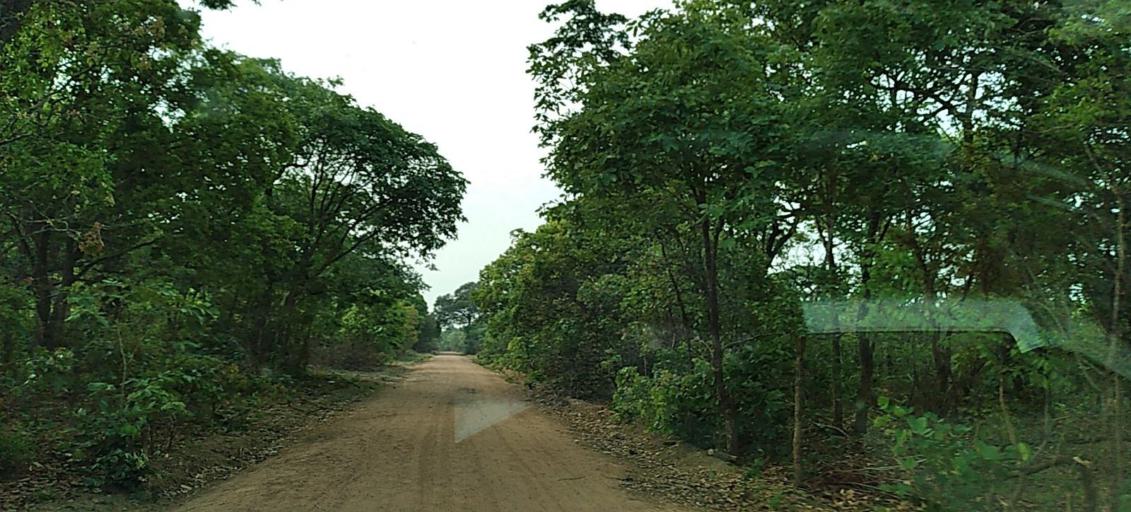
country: ZM
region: Copperbelt
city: Kalulushi
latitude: -12.9027
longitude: 27.6866
